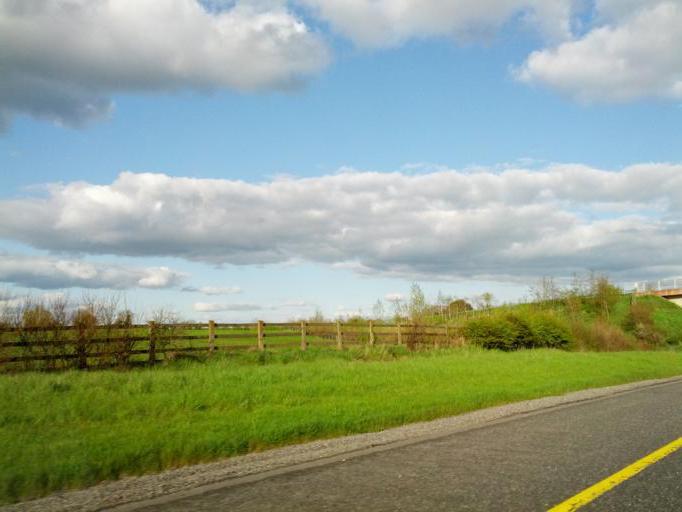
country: IE
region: Leinster
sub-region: An Iarmhi
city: Kinnegad
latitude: 53.4418
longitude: -7.0259
